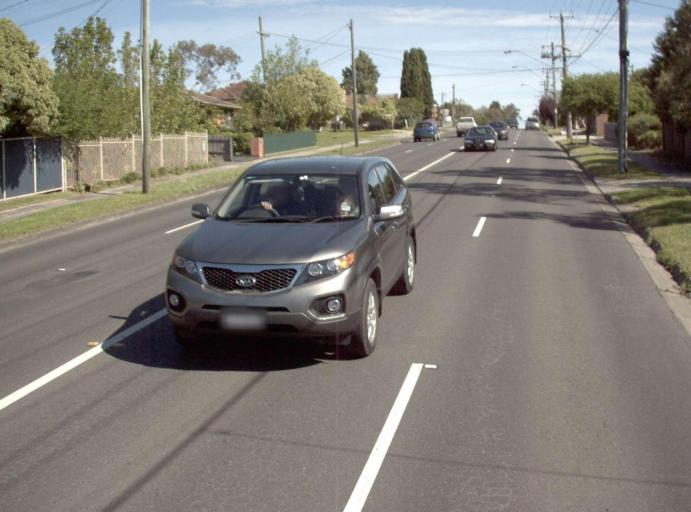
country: AU
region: Victoria
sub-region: Knox
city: Bayswater
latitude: -37.8538
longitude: 145.2683
